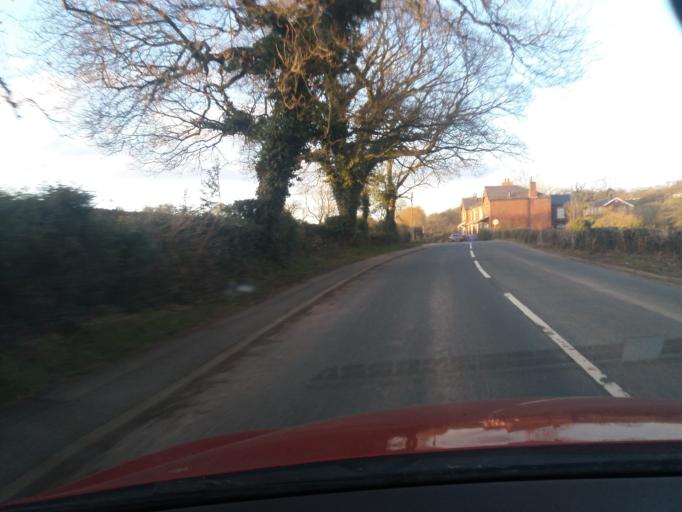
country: GB
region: England
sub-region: Lancashire
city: Chorley
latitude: 53.6772
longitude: -2.6216
